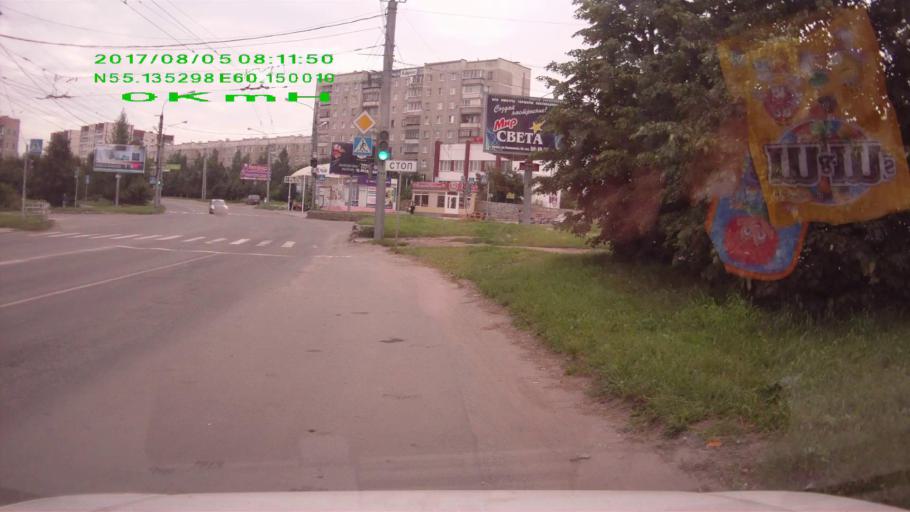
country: RU
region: Chelyabinsk
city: Turgoyak
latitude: 55.1353
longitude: 60.1500
